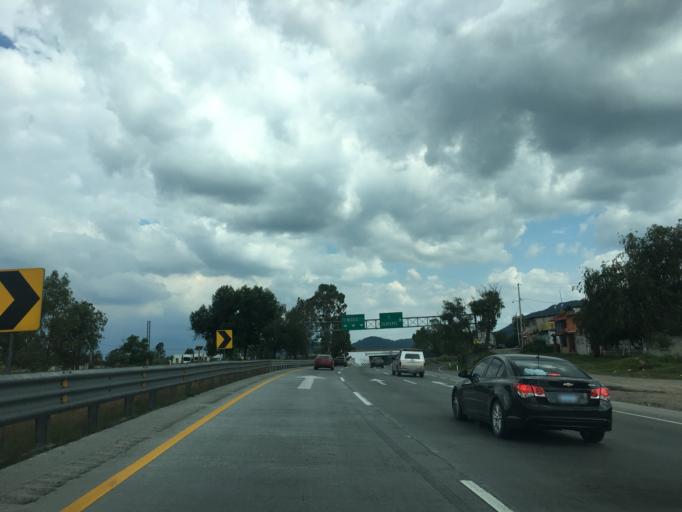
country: MX
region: Hidalgo
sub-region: Tepeji del Rio de Ocampo
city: Santiago Tlautla
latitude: 19.9833
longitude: -99.4403
